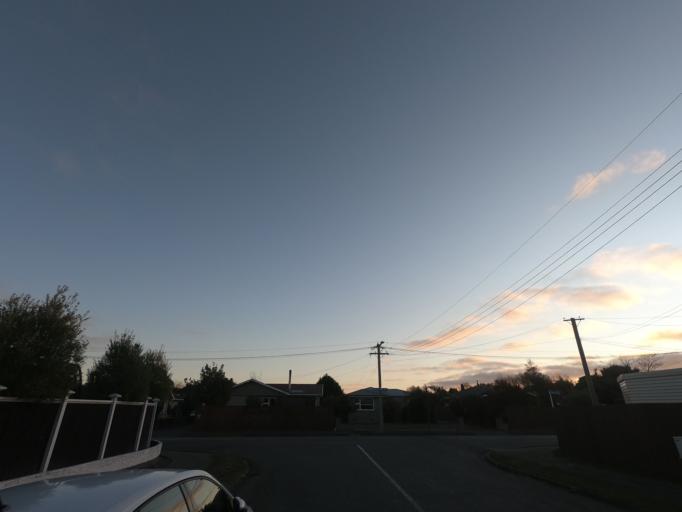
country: NZ
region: Canterbury
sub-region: Selwyn District
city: Prebbleton
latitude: -43.5761
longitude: 172.5600
